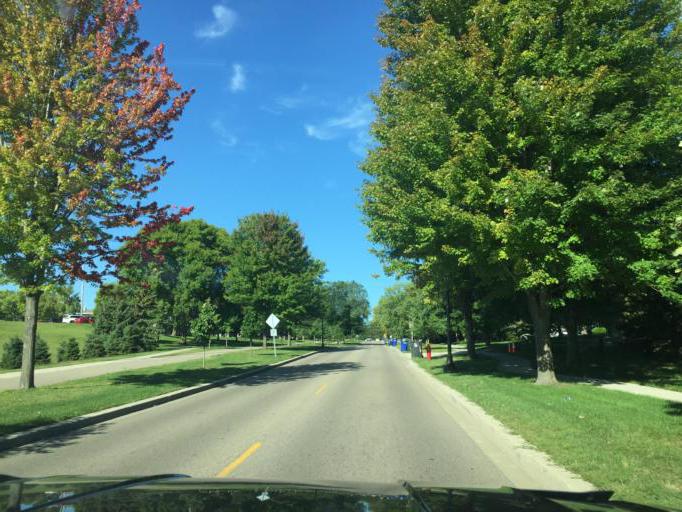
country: US
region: Minnesota
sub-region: Ramsey County
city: Little Canada
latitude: 44.9907
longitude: -93.0919
